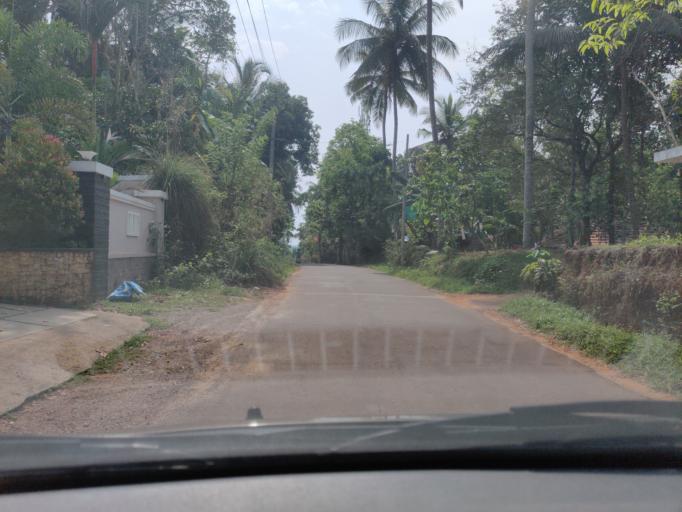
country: IN
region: Kerala
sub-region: Kozhikode
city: Kunnamangalam
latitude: 11.4196
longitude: 75.8717
